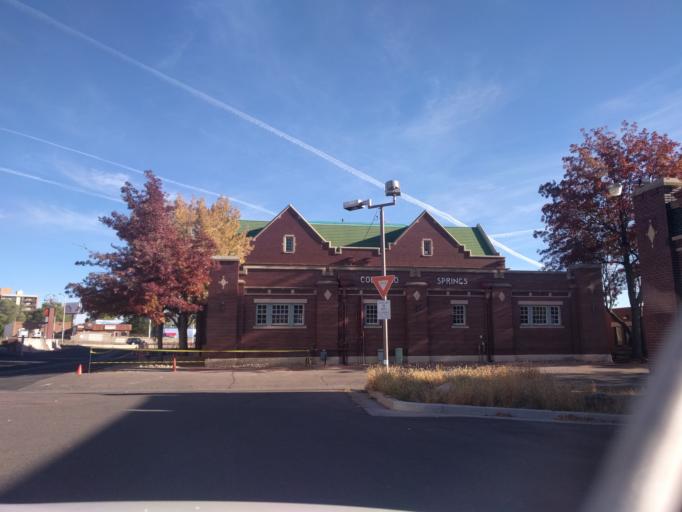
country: US
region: Colorado
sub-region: El Paso County
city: Colorado Springs
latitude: 38.8323
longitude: -104.8150
